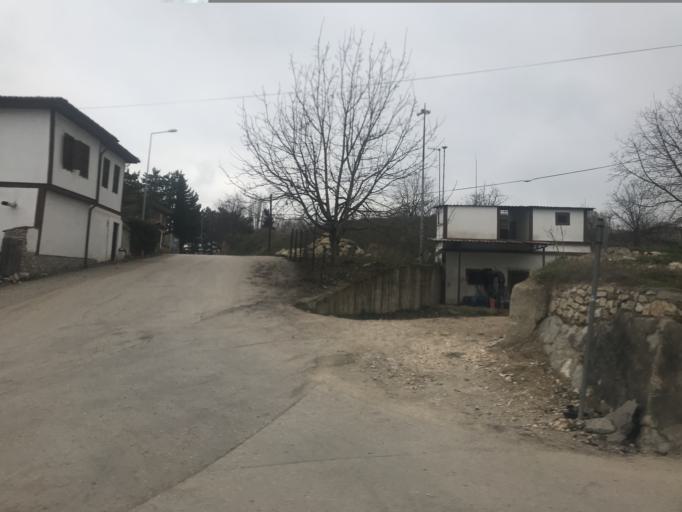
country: TR
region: Karabuk
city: Safranbolu
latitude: 41.2596
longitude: 32.6790
